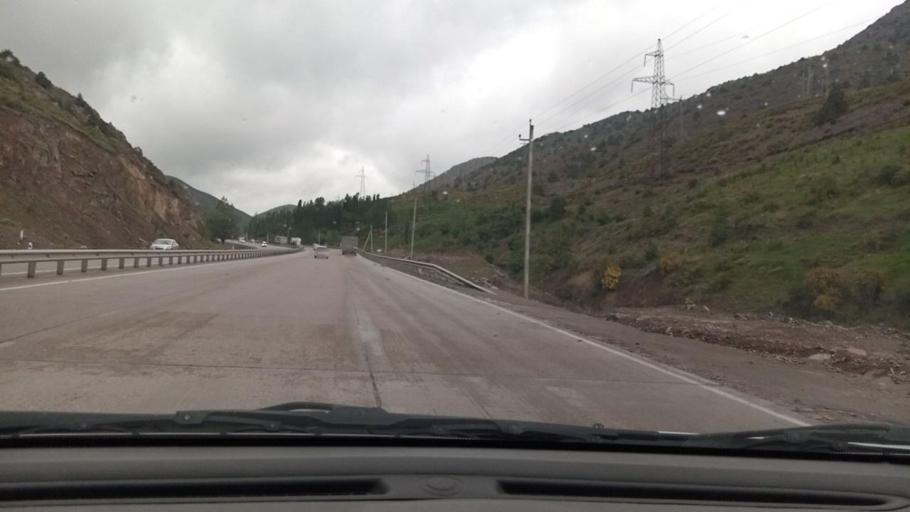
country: UZ
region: Toshkent
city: Angren
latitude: 41.0428
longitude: 70.5753
